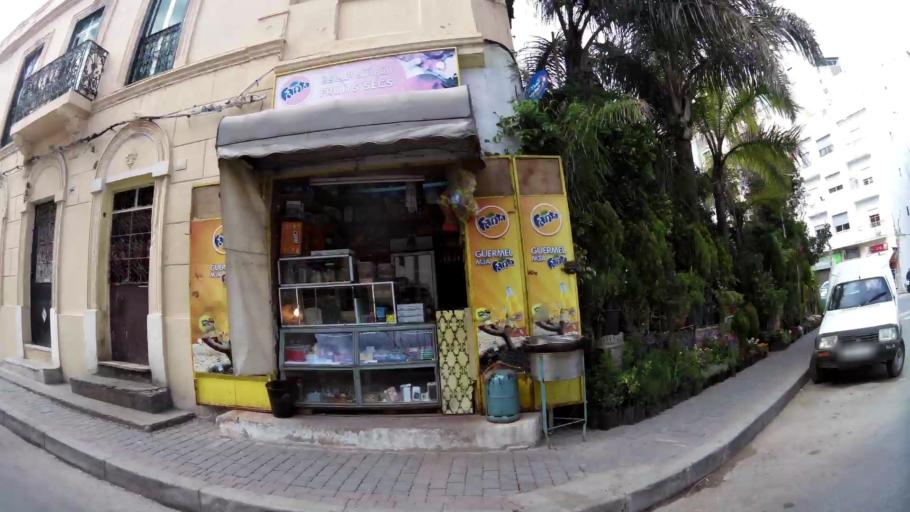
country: MA
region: Tanger-Tetouan
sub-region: Tanger-Assilah
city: Tangier
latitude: 35.7822
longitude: -5.8182
